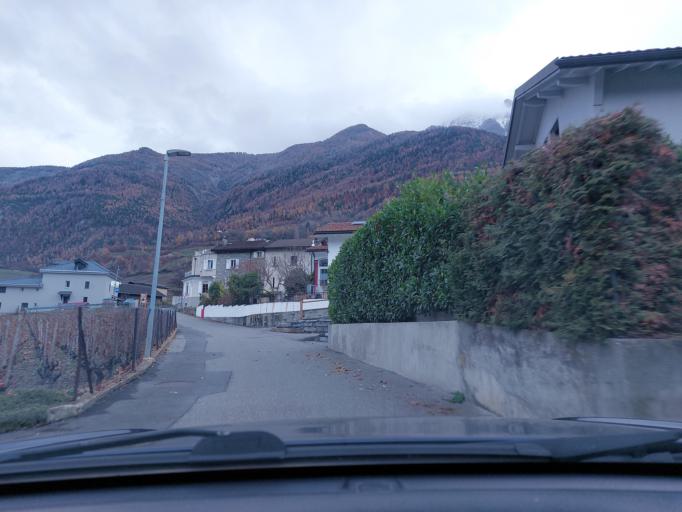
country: CH
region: Valais
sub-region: Martigny District
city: Saxon
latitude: 46.1473
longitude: 7.1778
